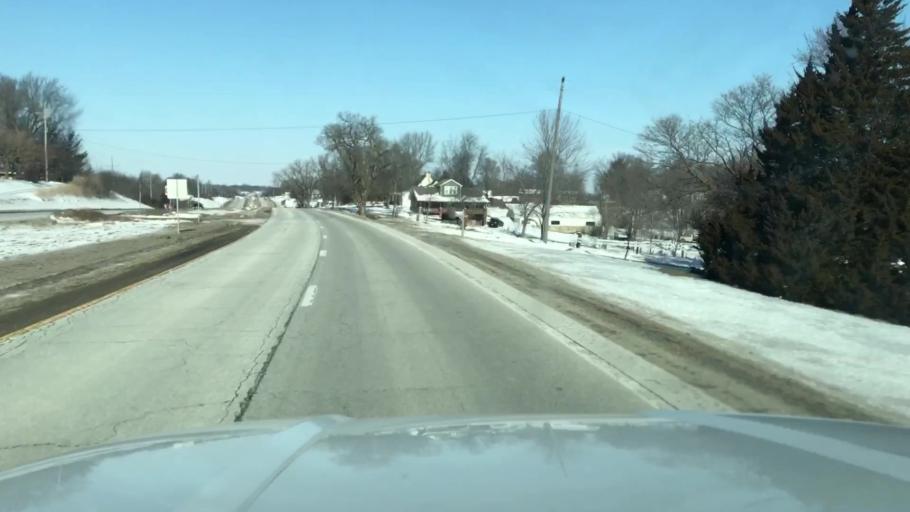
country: US
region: Missouri
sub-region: Andrew County
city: Savannah
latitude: 39.9117
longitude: -94.8095
